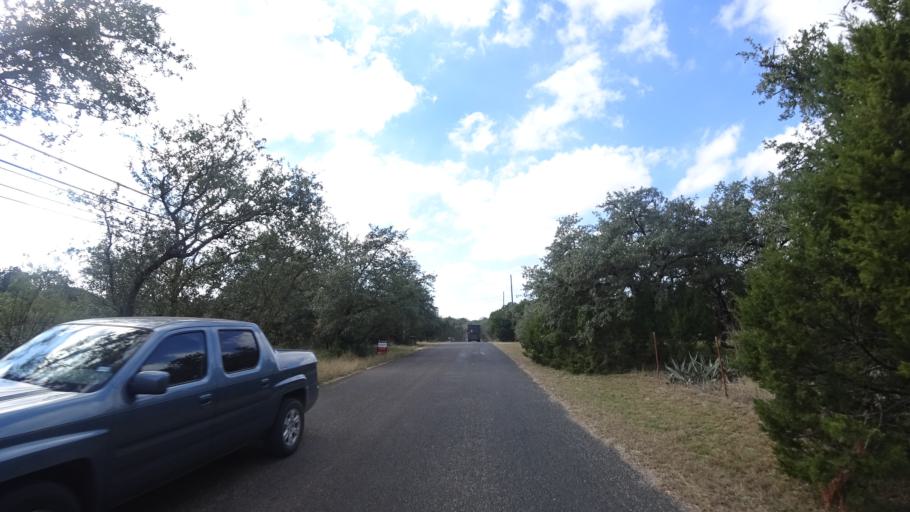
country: US
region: Texas
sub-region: Travis County
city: Shady Hollow
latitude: 30.1759
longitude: -97.8609
